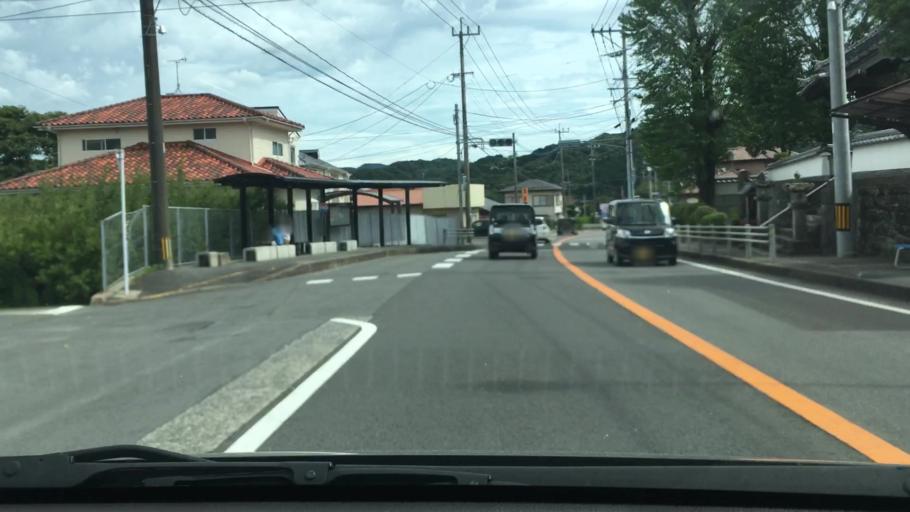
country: JP
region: Nagasaki
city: Togitsu
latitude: 32.8999
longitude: 129.7809
